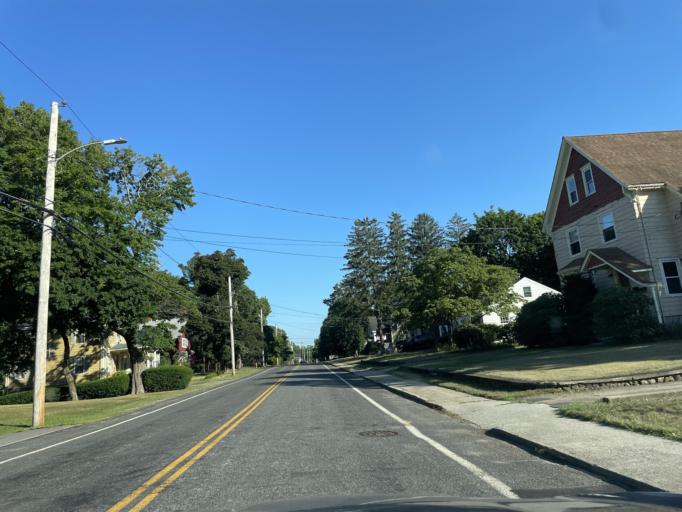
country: US
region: Massachusetts
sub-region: Bristol County
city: Mansfield
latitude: 42.0330
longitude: -71.2298
